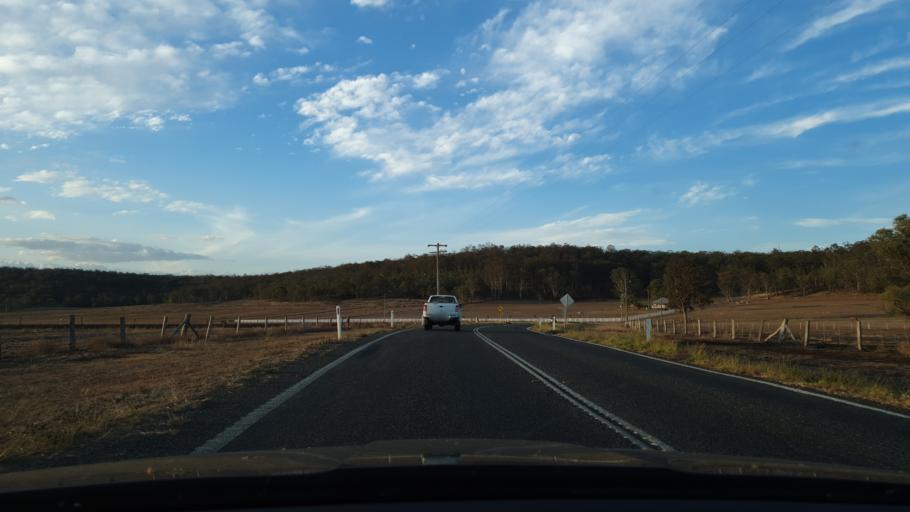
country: AU
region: Queensland
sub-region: Southern Downs
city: Warwick
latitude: -28.1885
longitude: 152.0090
